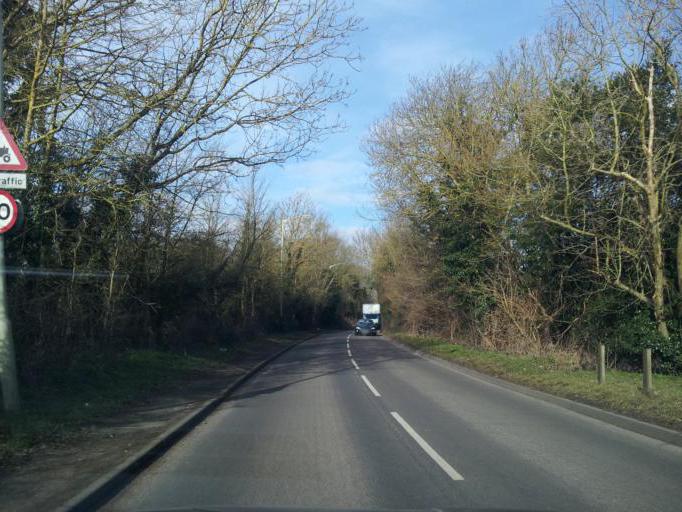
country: GB
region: England
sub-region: Hertfordshire
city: Shenley AV
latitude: 51.7445
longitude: -0.2762
